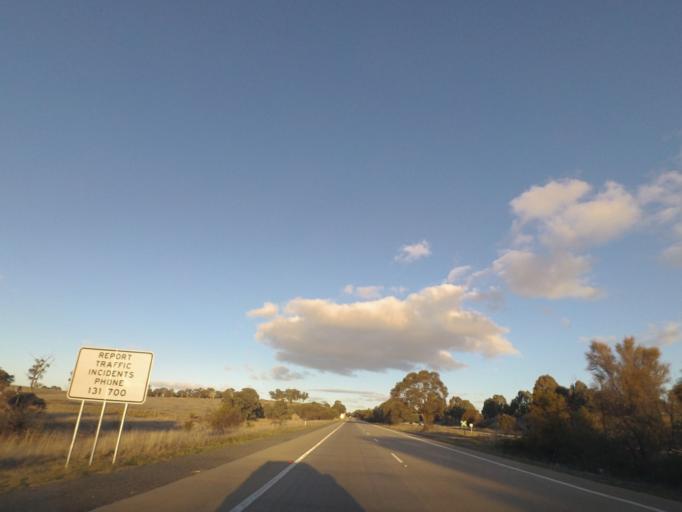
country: AU
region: New South Wales
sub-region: Yass Valley
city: Yass
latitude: -34.8084
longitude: 148.9313
